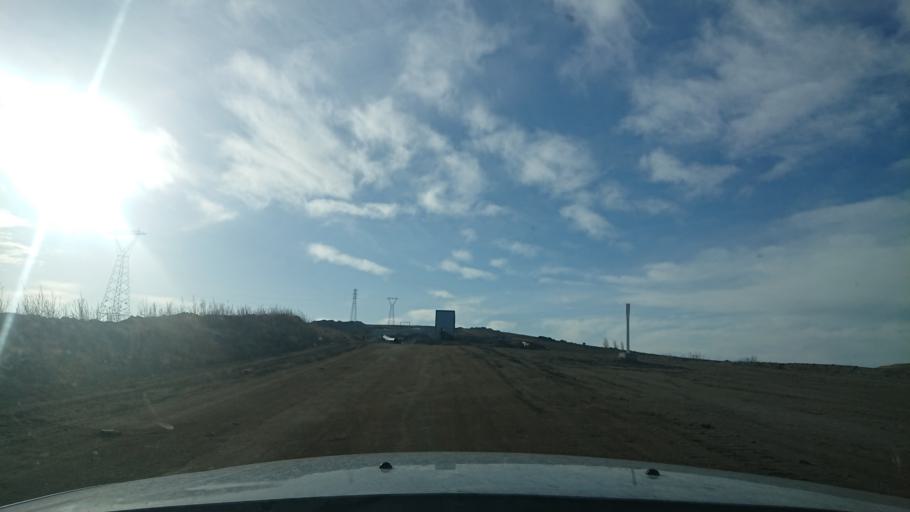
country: TR
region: Aksaray
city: Agacoren
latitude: 38.8493
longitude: 33.9432
